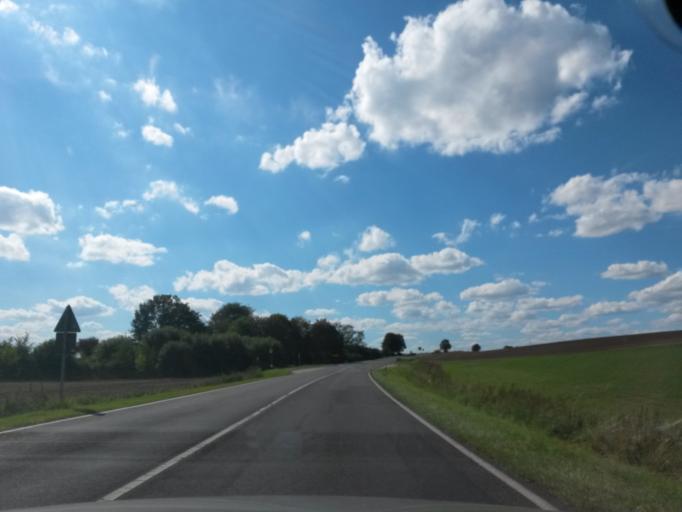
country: DE
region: Brandenburg
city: Meyenburg
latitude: 53.0261
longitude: 14.2043
